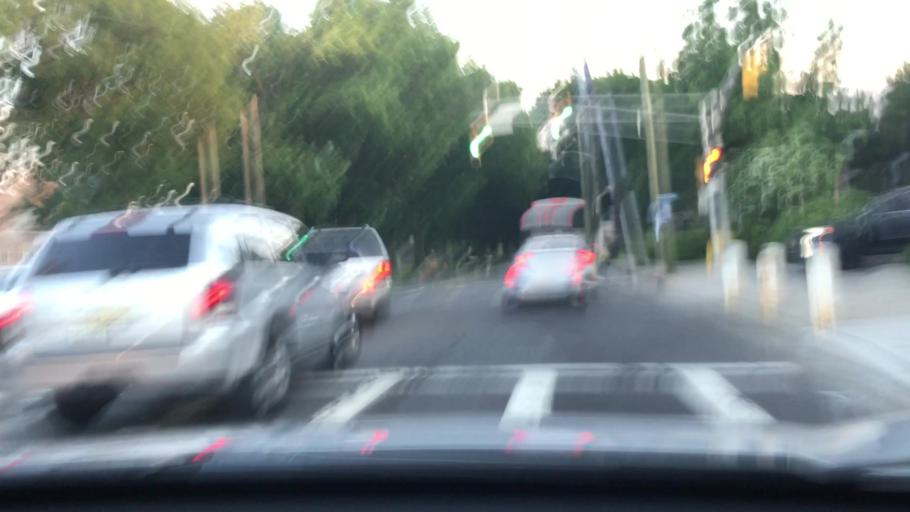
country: US
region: New Jersey
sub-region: Bergen County
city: Bergenfield
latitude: 40.9123
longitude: -73.9978
